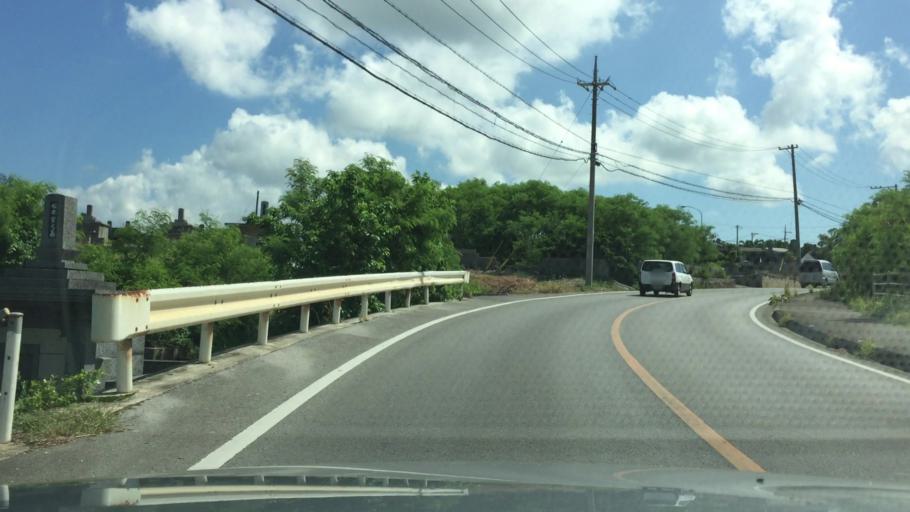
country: JP
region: Okinawa
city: Ishigaki
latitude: 24.3501
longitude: 124.1709
